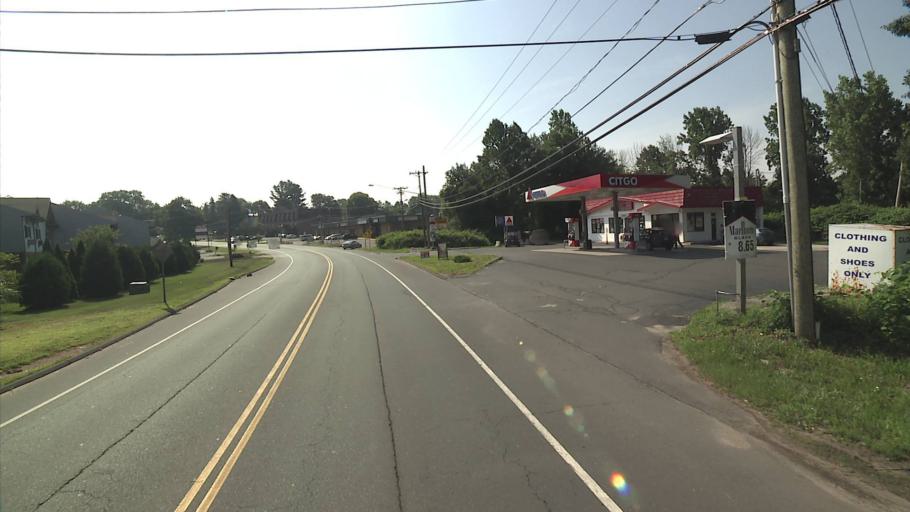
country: US
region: Connecticut
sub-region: New Haven County
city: Wolcott
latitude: 41.5526
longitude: -72.9881
